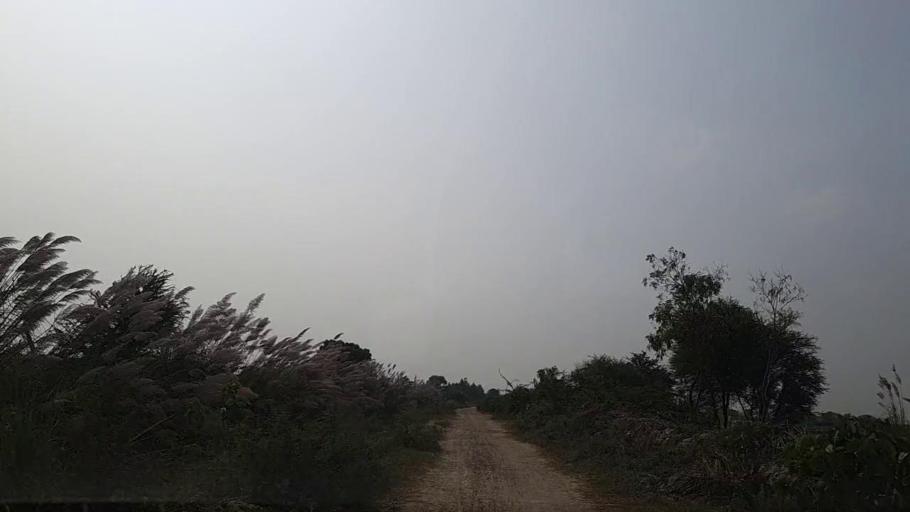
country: PK
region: Sindh
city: Thatta
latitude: 24.6565
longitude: 67.7696
